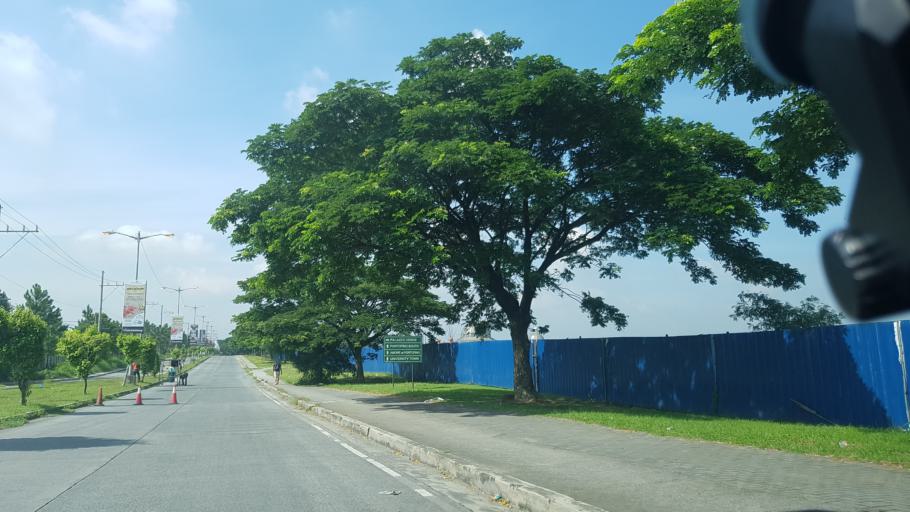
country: PH
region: Calabarzon
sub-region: Province of Laguna
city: San Pedro
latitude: 14.3736
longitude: 121.0122
